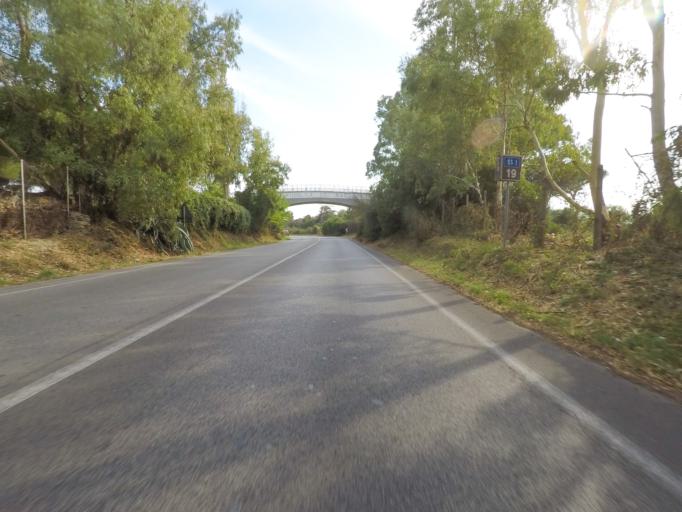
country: IT
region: Latium
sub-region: Citta metropolitana di Roma Capitale
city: Civitavecchia
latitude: 42.0597
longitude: 11.8171
